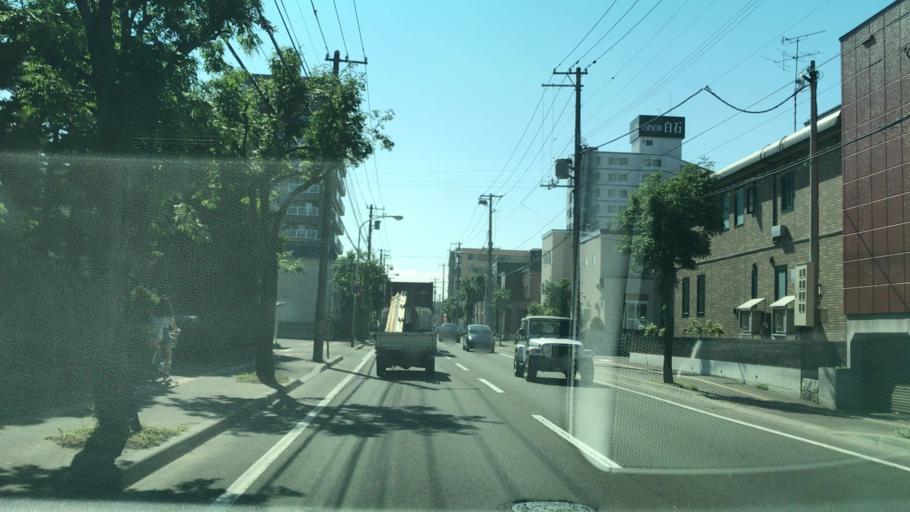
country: JP
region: Hokkaido
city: Sapporo
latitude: 43.0536
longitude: 141.4089
